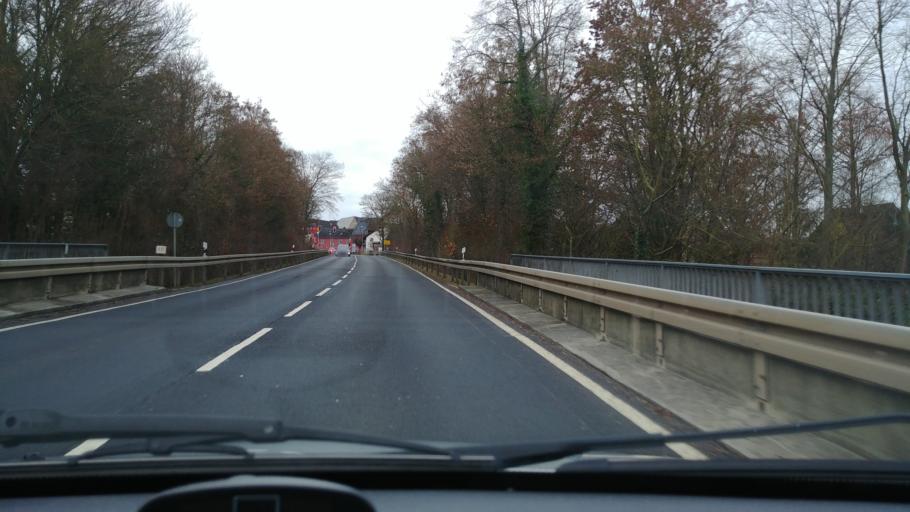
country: DE
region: Rheinland-Pfalz
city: Netzbach
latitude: 50.3109
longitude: 8.1590
